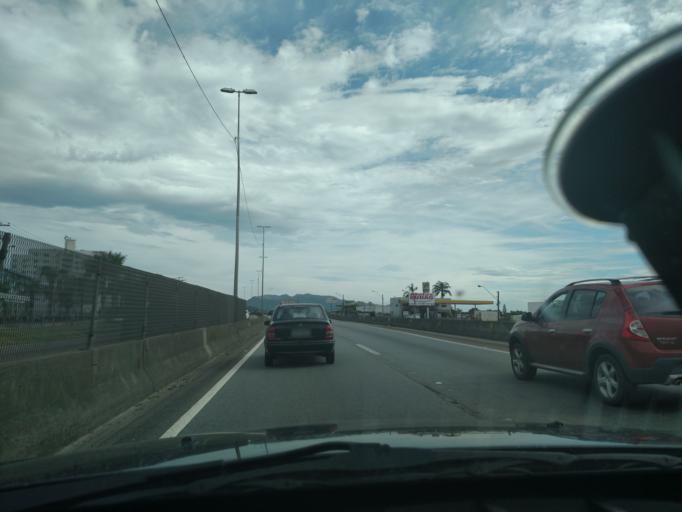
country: BR
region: Santa Catarina
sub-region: Sao Jose
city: Campinas
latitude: -27.5439
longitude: -48.6205
